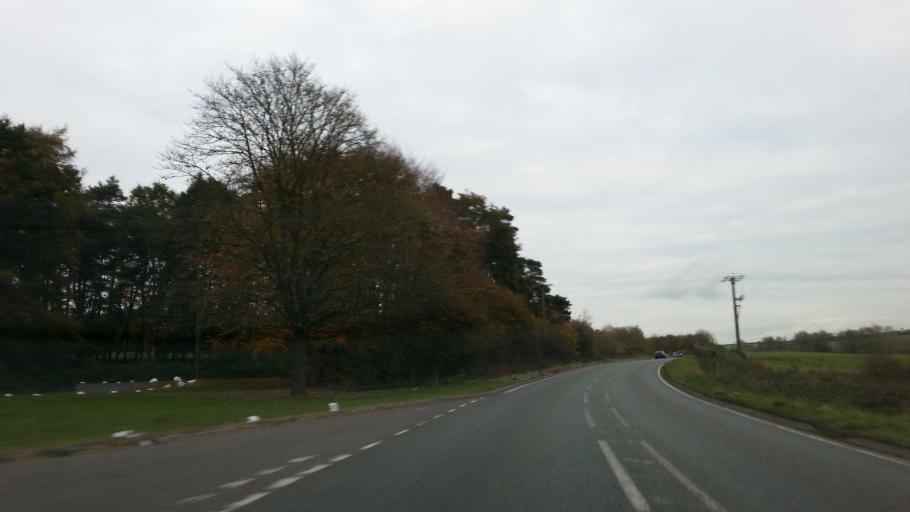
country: GB
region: England
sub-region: Northamptonshire
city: Corby
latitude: 52.5097
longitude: -0.6084
